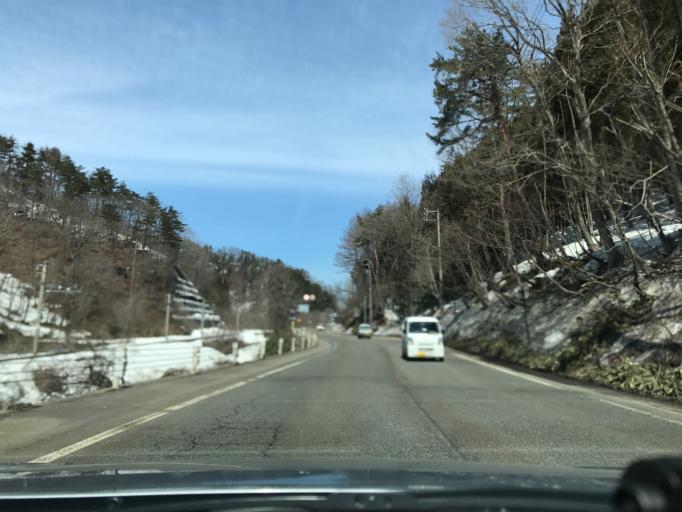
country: JP
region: Nagano
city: Omachi
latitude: 36.5861
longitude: 137.8411
